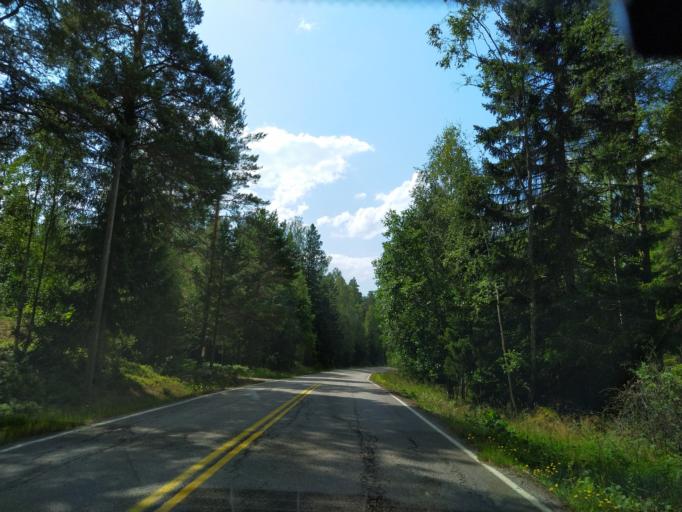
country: FI
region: Uusimaa
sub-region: Helsinki
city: Kirkkonummi
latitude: 60.0309
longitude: 24.4846
